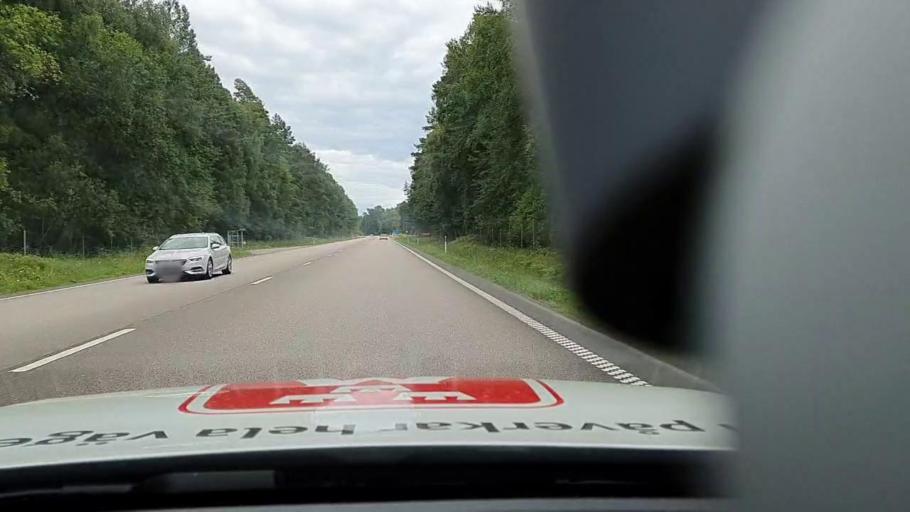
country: SE
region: Vaestra Goetaland
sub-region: Lidkopings Kommun
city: Vinninga
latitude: 58.4351
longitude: 13.2821
